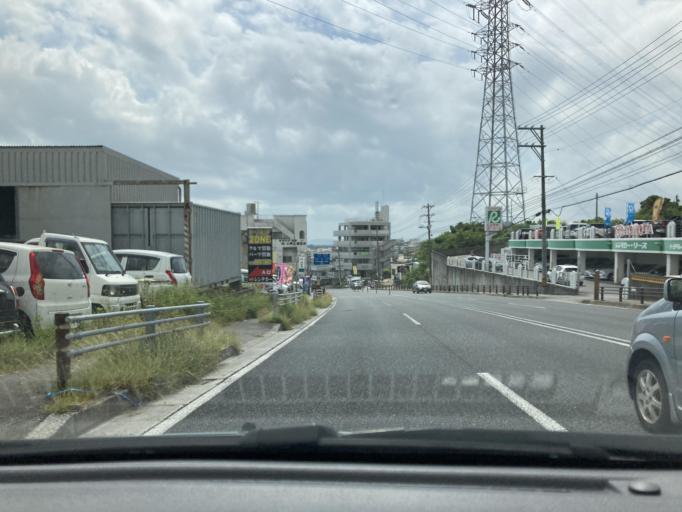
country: JP
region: Okinawa
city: Okinawa
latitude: 26.3293
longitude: 127.8223
